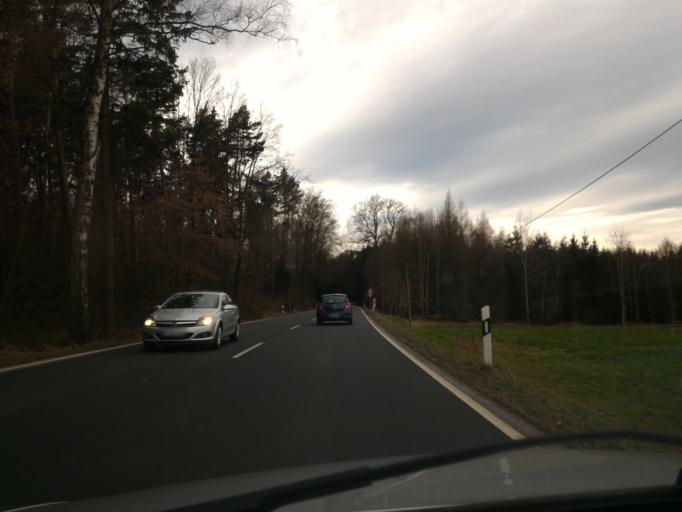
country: DE
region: Saxony
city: Durrrohrsdorf
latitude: 51.0662
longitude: 13.9886
